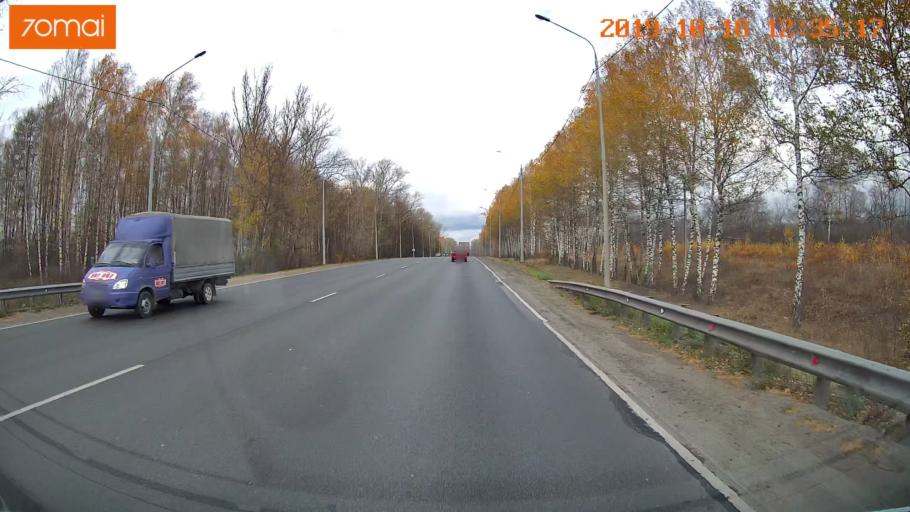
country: RU
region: Rjazan
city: Ryazan'
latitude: 54.6227
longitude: 39.6360
